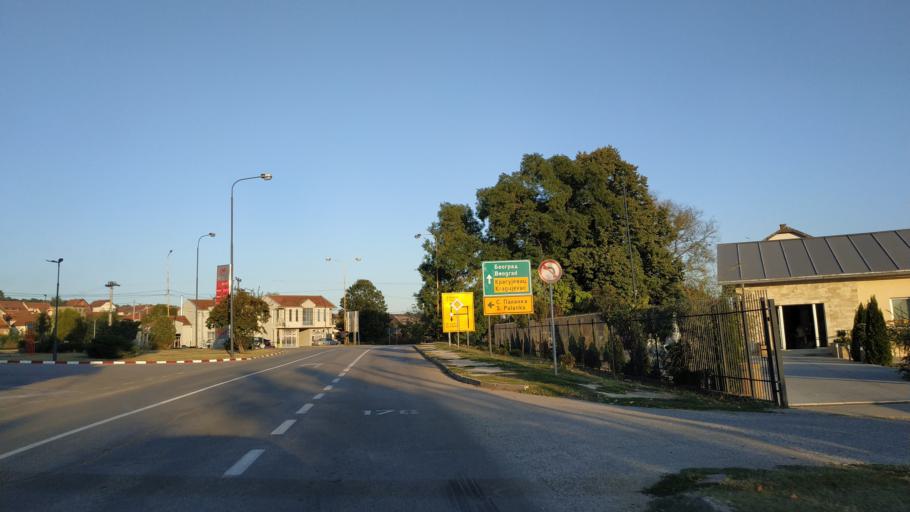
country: RS
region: Central Serbia
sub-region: Sumadijski Okrug
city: Raca
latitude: 44.2313
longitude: 20.9710
